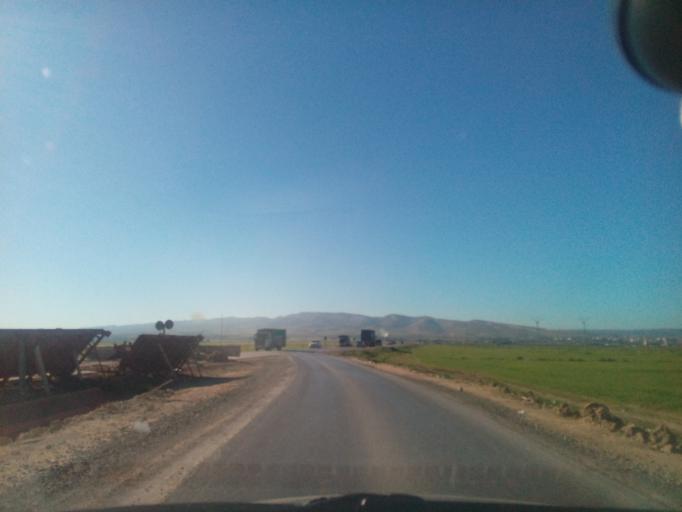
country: DZ
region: Relizane
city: Relizane
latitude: 35.8978
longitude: 0.5607
